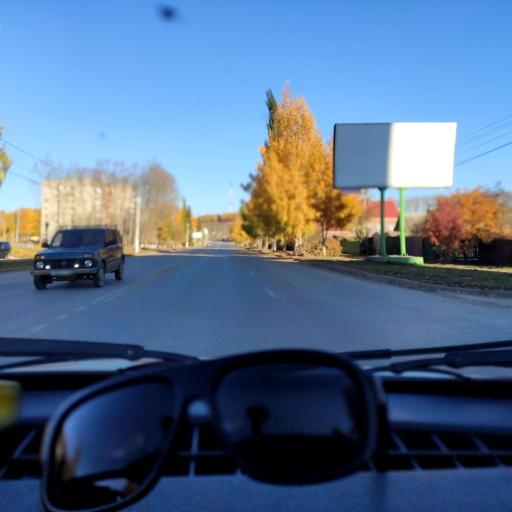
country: RU
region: Bashkortostan
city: Blagoveshchensk
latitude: 55.0524
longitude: 55.9519
